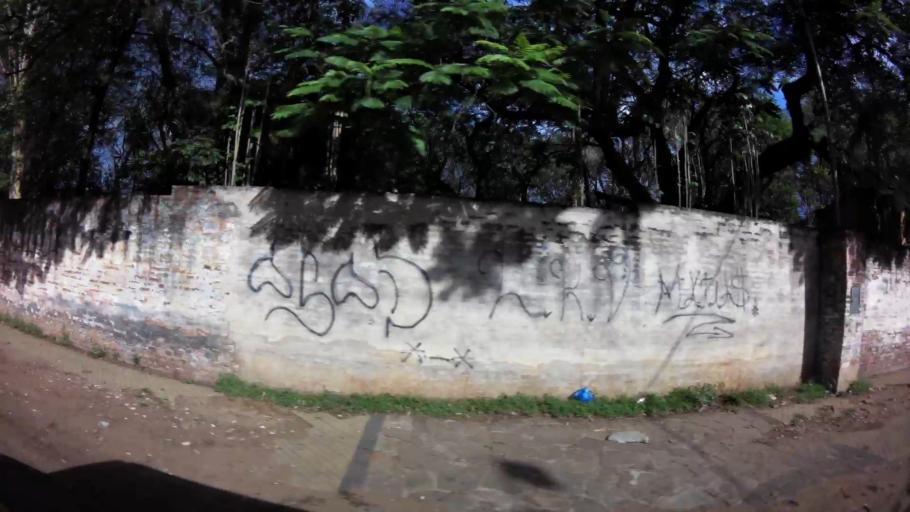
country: PY
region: Central
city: Villa Elisa
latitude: -25.3397
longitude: -57.5642
